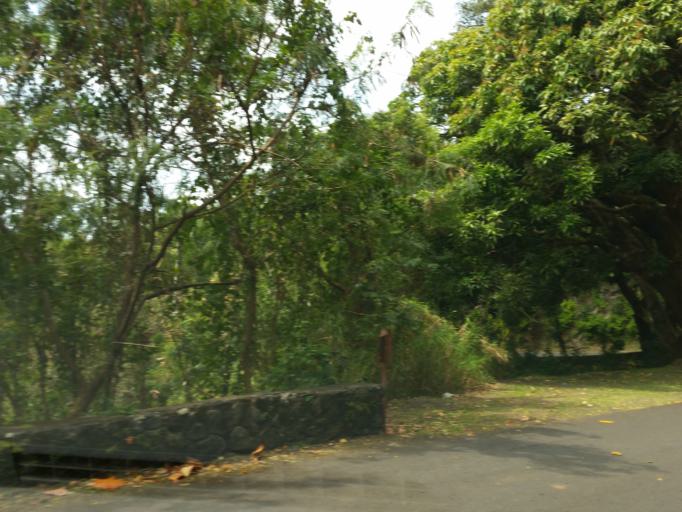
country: RE
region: Reunion
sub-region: Reunion
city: Sainte-Suzanne
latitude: -20.9249
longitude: 55.6058
